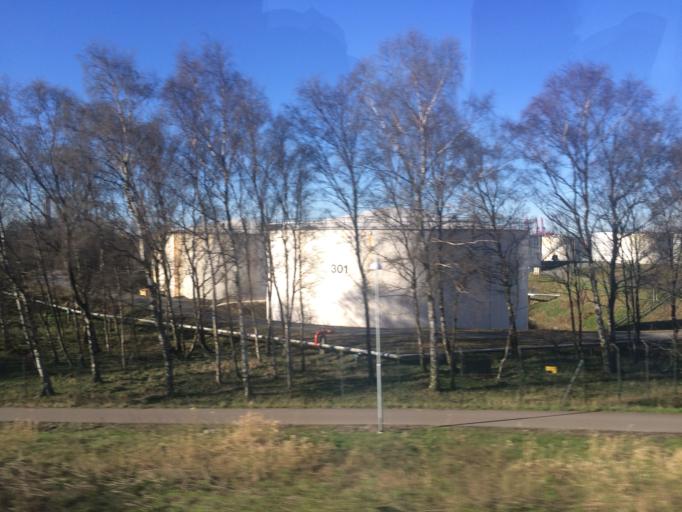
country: SE
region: Vaestra Goetaland
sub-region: Goteborg
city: Majorna
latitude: 57.7043
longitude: 11.8909
